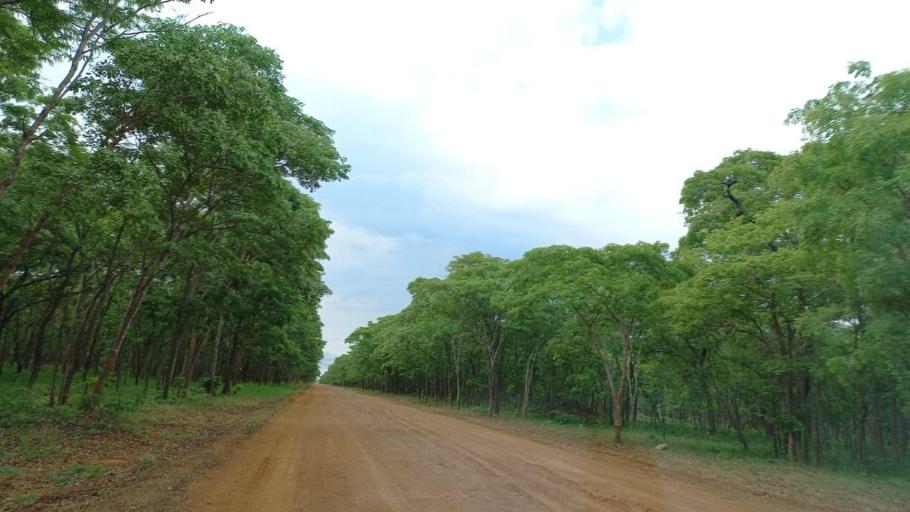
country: ZM
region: North-Western
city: Kalengwa
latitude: -13.3589
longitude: 25.0762
